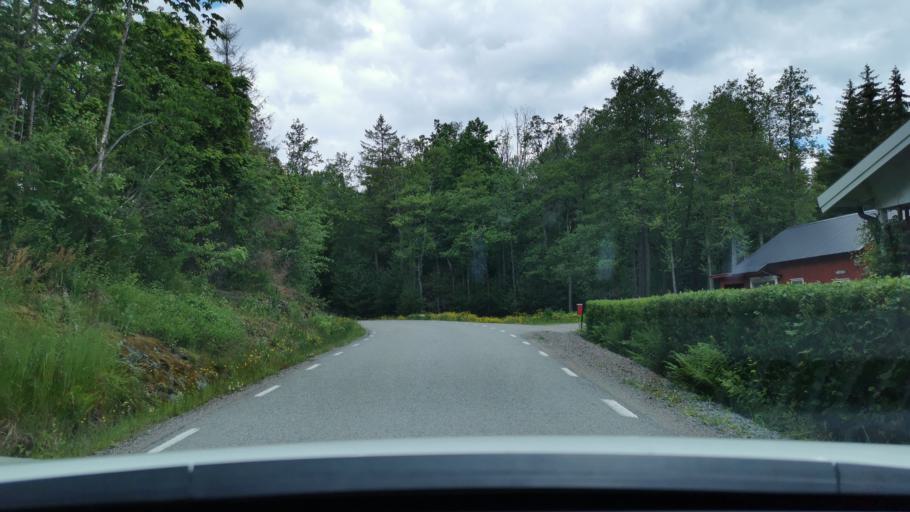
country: SE
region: Vaestra Goetaland
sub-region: Bengtsfors Kommun
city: Dals Langed
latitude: 58.8011
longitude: 12.3286
